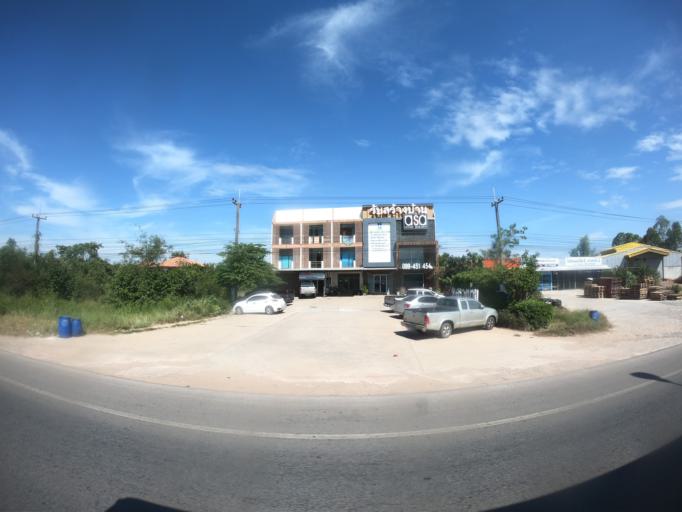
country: TH
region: Khon Kaen
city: Khon Kaen
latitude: 16.3881
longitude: 102.8345
